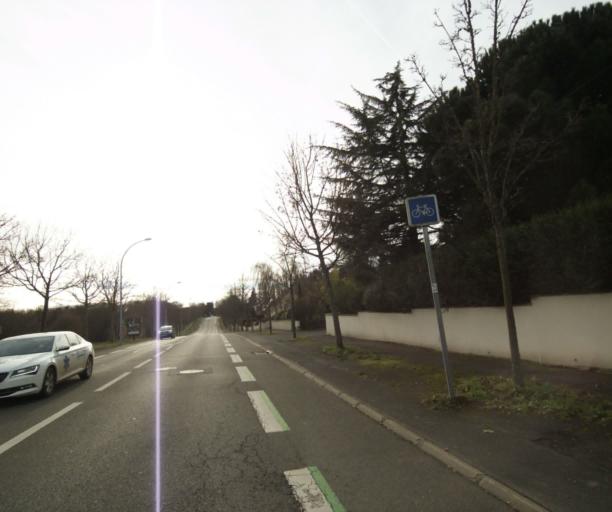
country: FR
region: Pays de la Loire
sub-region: Departement de la Sarthe
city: Sarge-les-le-Mans
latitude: 48.0078
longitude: 0.2276
